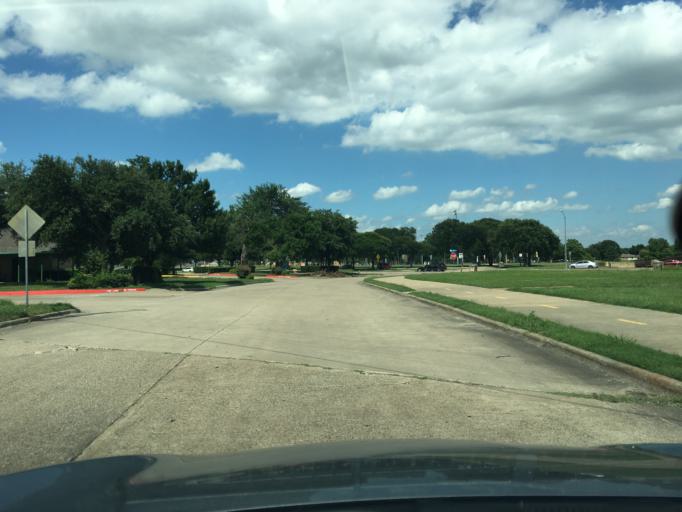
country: US
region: Texas
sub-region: Dallas County
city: Richardson
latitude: 32.9488
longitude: -96.7009
